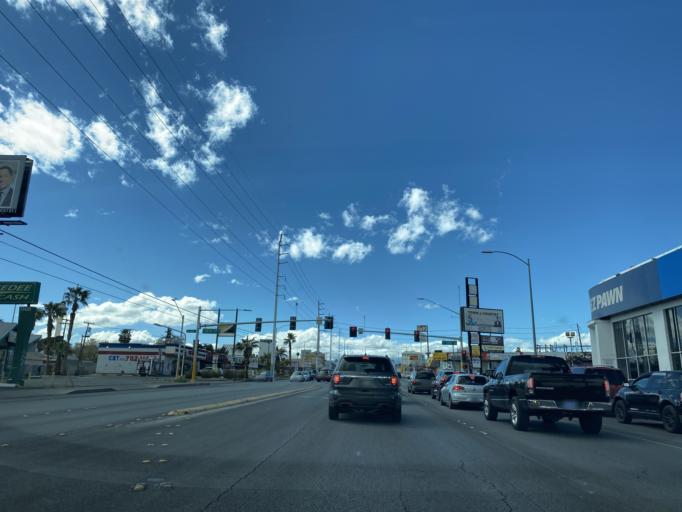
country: US
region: Nevada
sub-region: Clark County
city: Las Vegas
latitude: 36.1589
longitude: -115.1320
